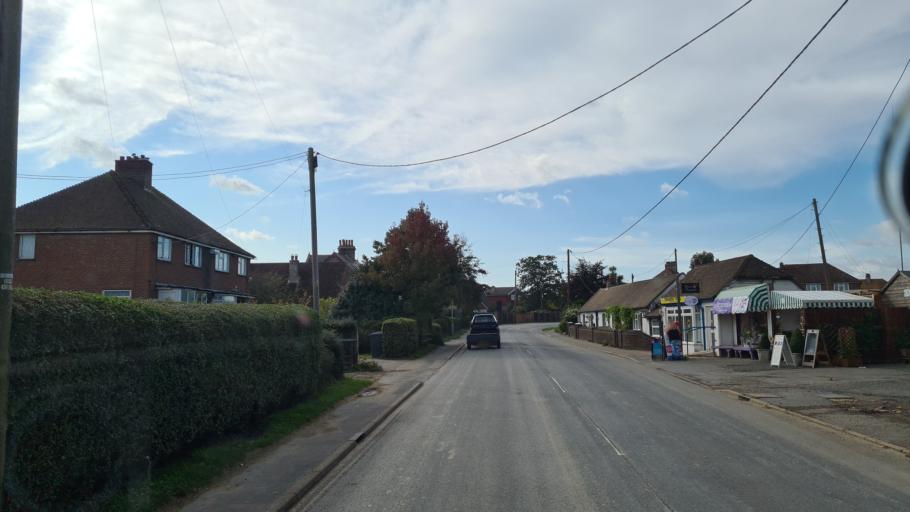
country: GB
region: England
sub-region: East Sussex
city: Hailsham
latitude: 50.8782
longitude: 0.2690
